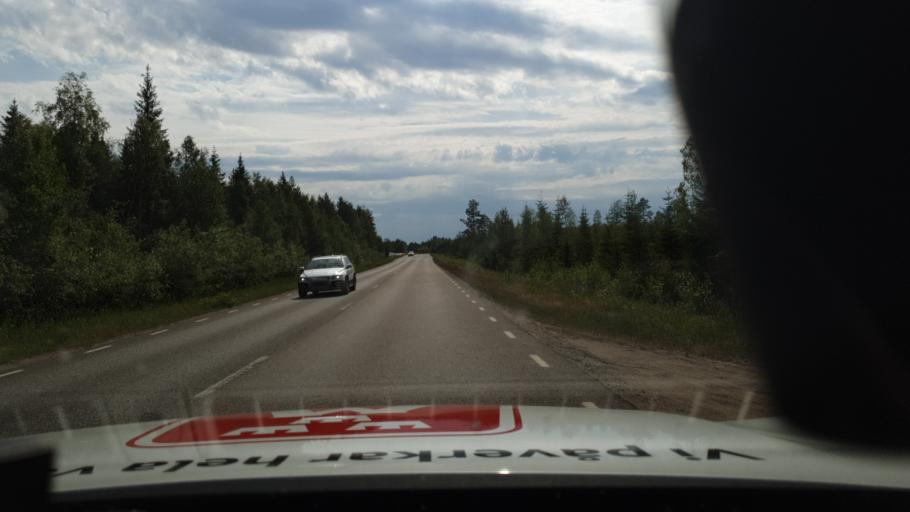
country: SE
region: Norrbotten
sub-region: Lulea Kommun
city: Ranea
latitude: 65.8451
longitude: 22.2664
